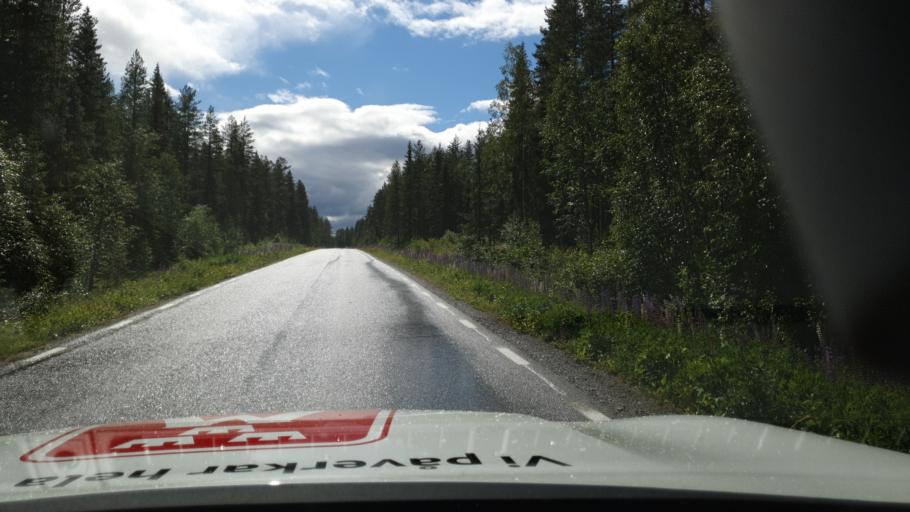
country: SE
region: Vaesterbotten
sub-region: Bjurholms Kommun
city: Bjurholm
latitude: 63.9760
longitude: 19.3181
